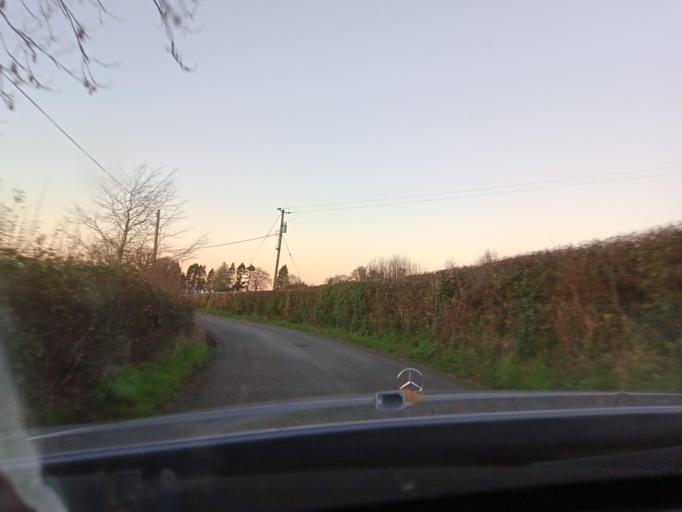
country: IE
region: Leinster
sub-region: Kilkenny
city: Thomastown
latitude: 52.4692
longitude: -7.0978
